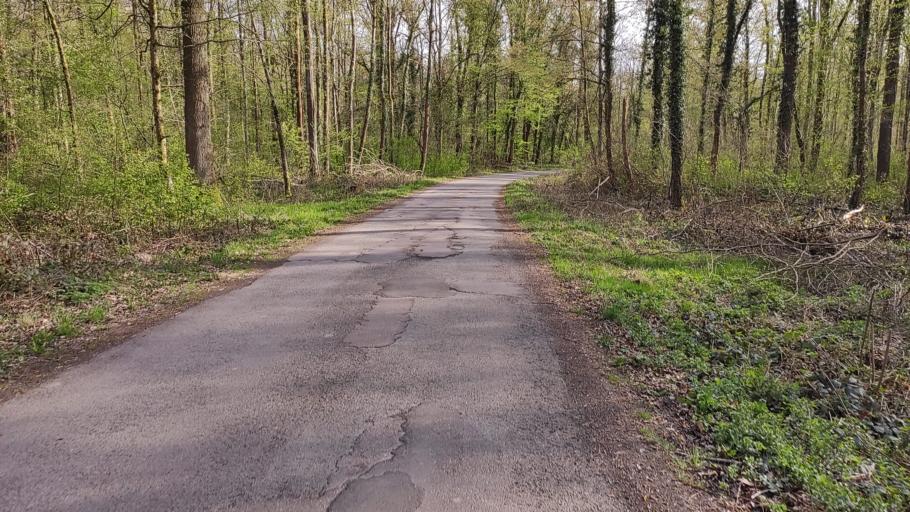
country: DE
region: Baden-Wuerttemberg
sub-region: Freiburg Region
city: Schallstadt
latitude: 47.9870
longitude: 7.7595
